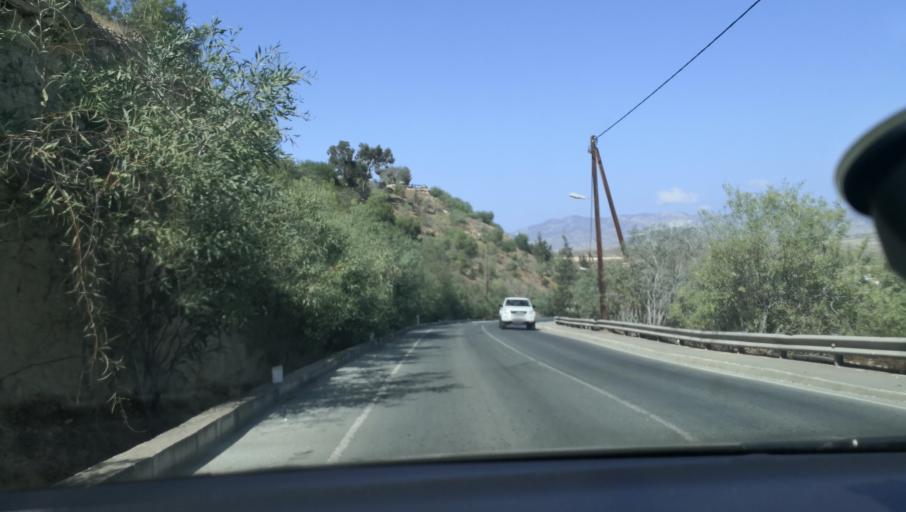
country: CY
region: Lefkosia
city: Mammari
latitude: 35.1697
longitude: 33.2021
